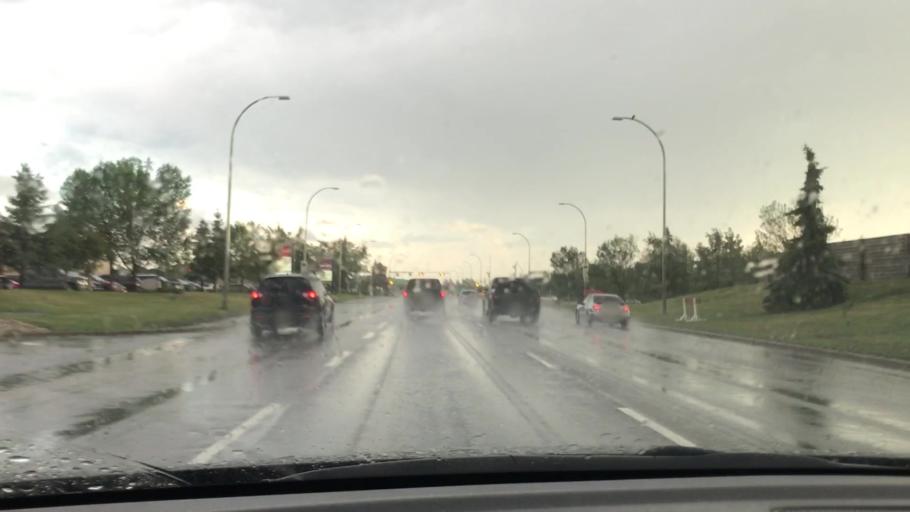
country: CA
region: Alberta
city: Edmonton
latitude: 53.4696
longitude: -113.4957
